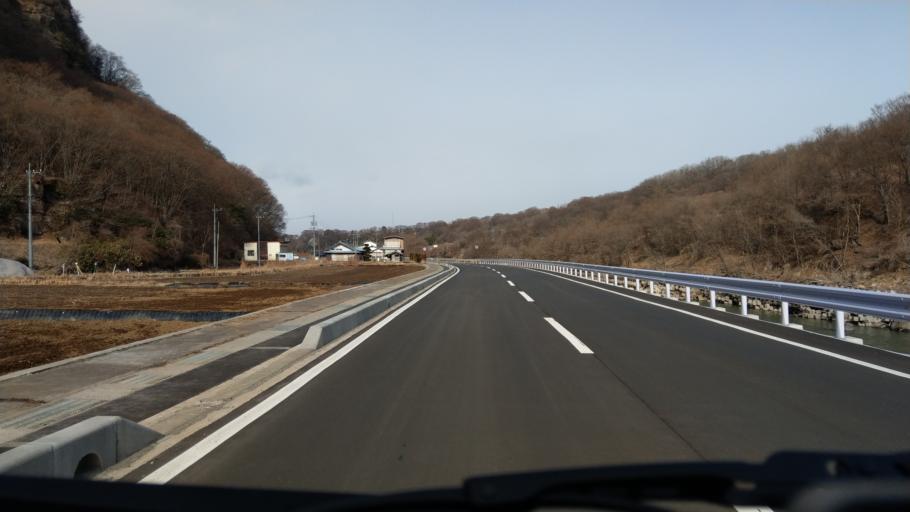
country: JP
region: Nagano
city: Komoro
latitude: 36.3327
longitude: 138.3878
